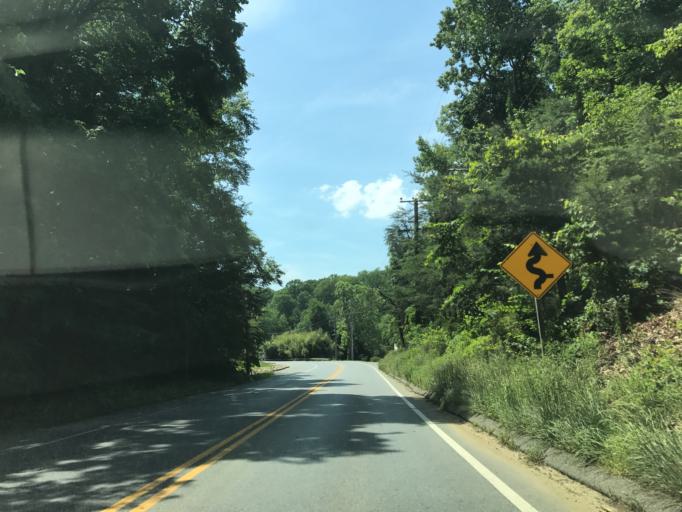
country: US
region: Maryland
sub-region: Anne Arundel County
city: Edgewater
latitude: 38.9868
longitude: -76.5655
